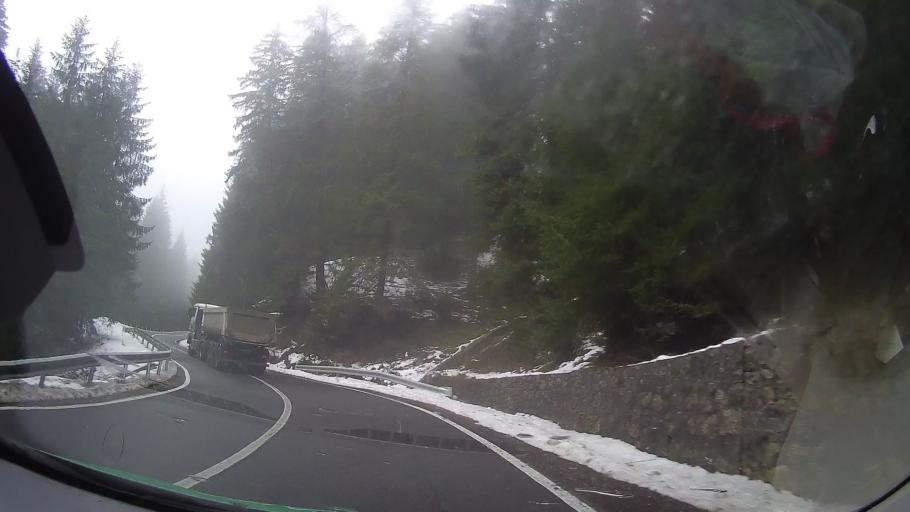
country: RO
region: Harghita
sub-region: Municipiul Gheorgheni
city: Gheorgheni
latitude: 46.7761
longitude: 25.7329
